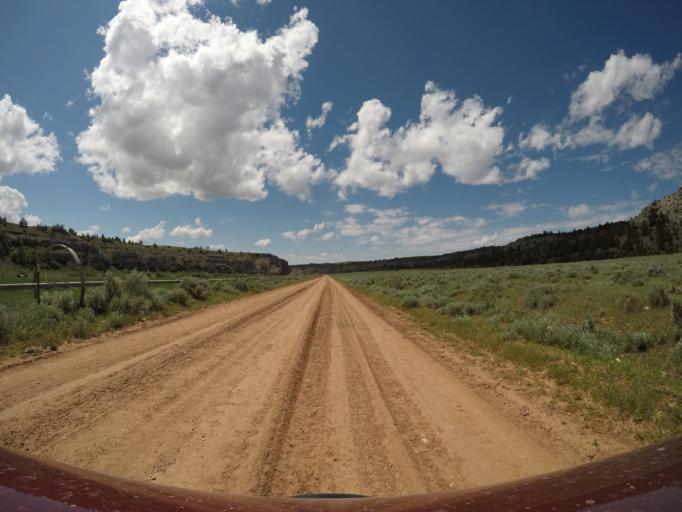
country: US
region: Montana
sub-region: Yellowstone County
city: Laurel
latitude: 45.2397
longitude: -108.6333
